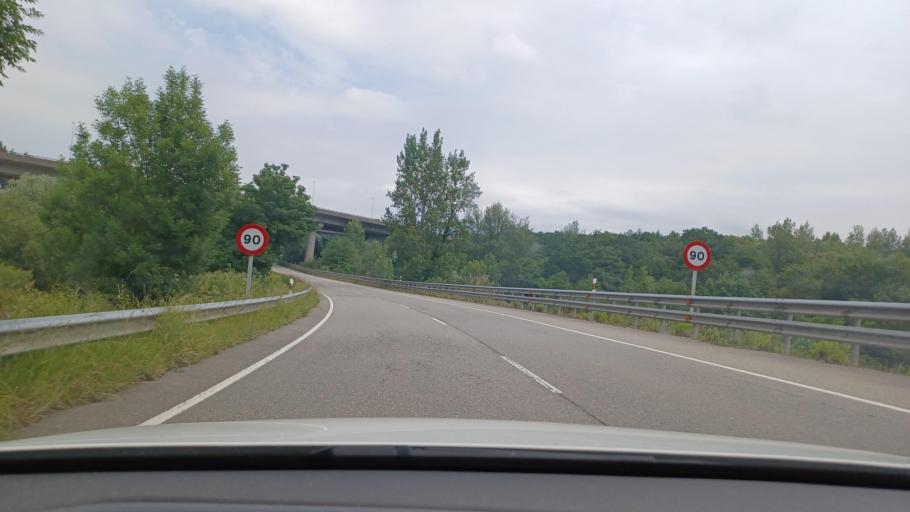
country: ES
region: Asturias
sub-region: Province of Asturias
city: Oviedo
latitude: 43.3441
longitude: -5.8630
